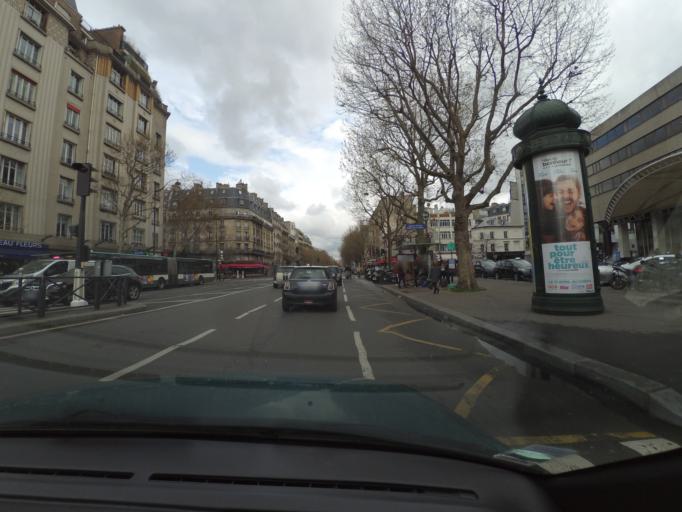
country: FR
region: Ile-de-France
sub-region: Departement des Hauts-de-Seine
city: Levallois-Perret
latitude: 48.8808
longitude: 2.2845
